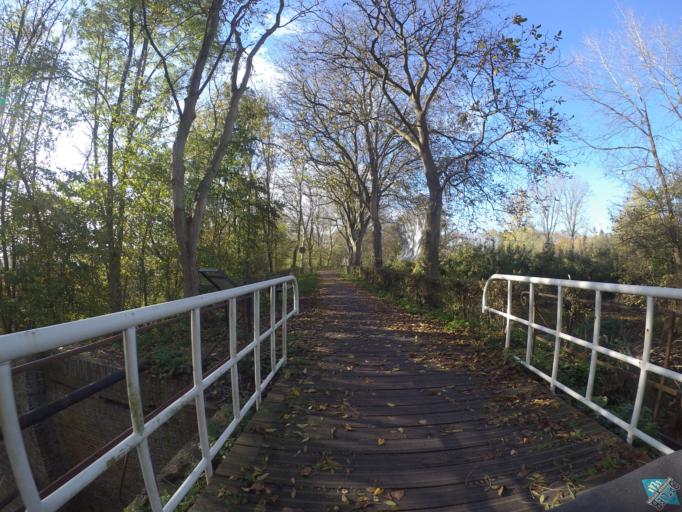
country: NL
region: North Brabant
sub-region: Gemeente Waalwijk
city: Waalwijk
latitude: 51.7204
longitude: 5.0933
